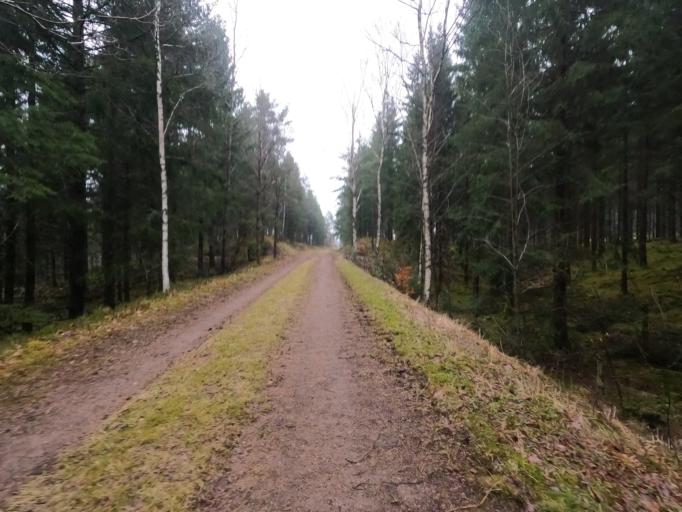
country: SE
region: Halland
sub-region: Hylte Kommun
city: Hyltebruk
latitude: 56.8030
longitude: 13.2571
